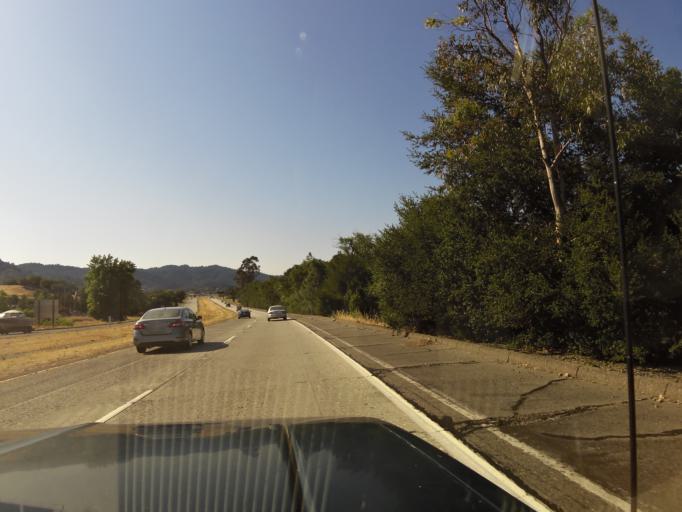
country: US
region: California
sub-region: Sonoma County
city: Cloverdale
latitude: 38.7739
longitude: -123.0000
